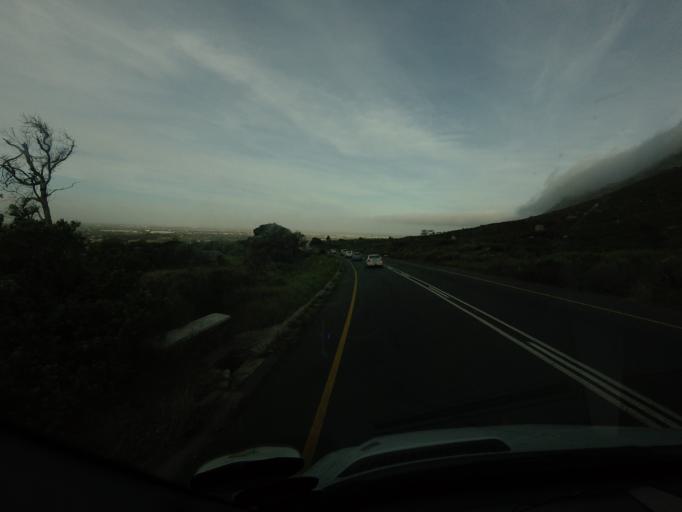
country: ZA
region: Western Cape
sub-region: City of Cape Town
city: Bergvliet
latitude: -34.0831
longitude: 18.4264
